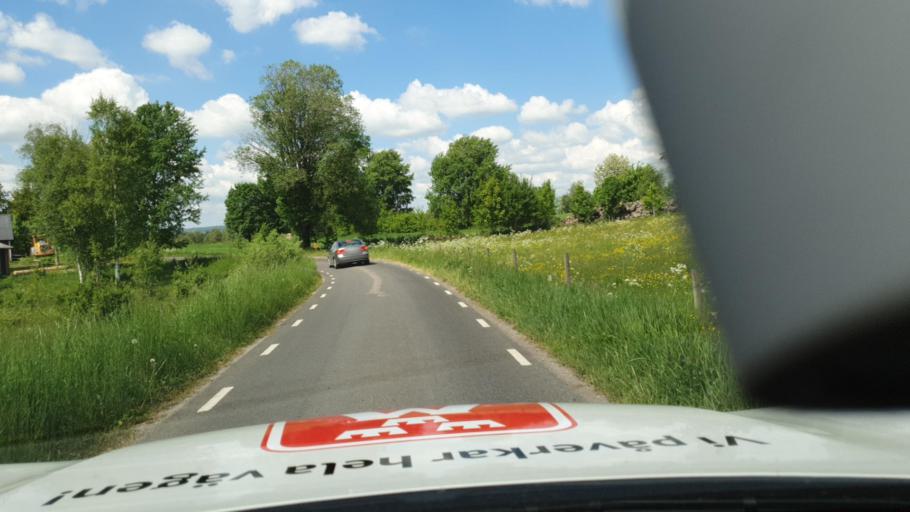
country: SE
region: Vaestra Goetaland
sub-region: Falkopings Kommun
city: Falkoeping
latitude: 58.0684
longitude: 13.6534
